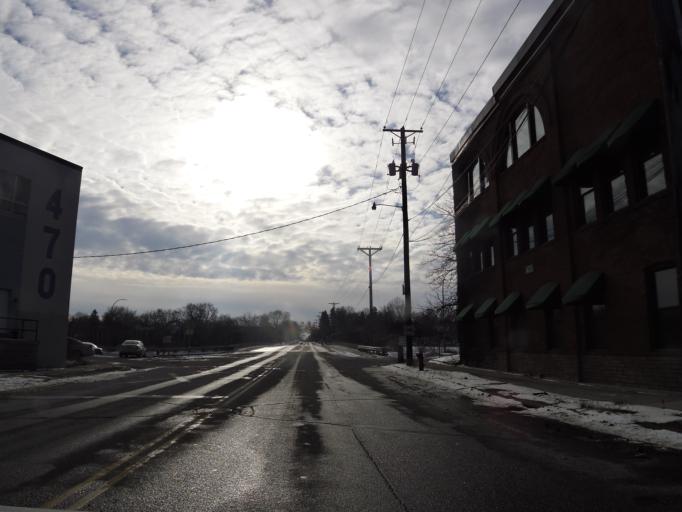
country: US
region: Minnesota
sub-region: Ramsey County
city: Falcon Heights
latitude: 44.9554
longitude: -93.1874
